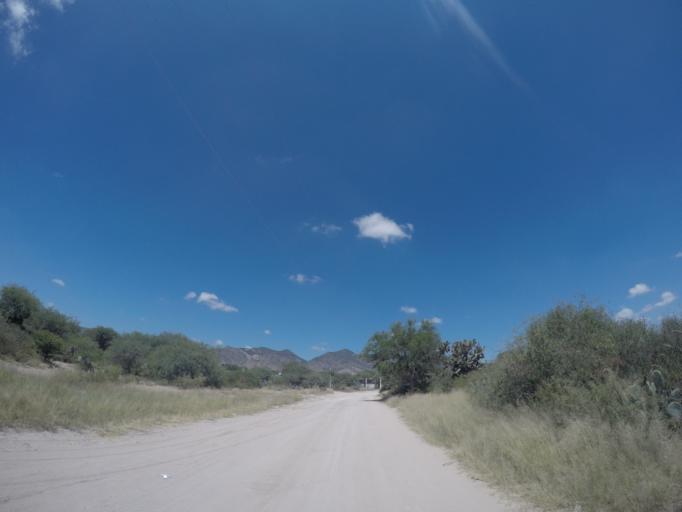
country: MX
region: San Luis Potosi
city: La Pila
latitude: 21.9809
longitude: -100.8982
